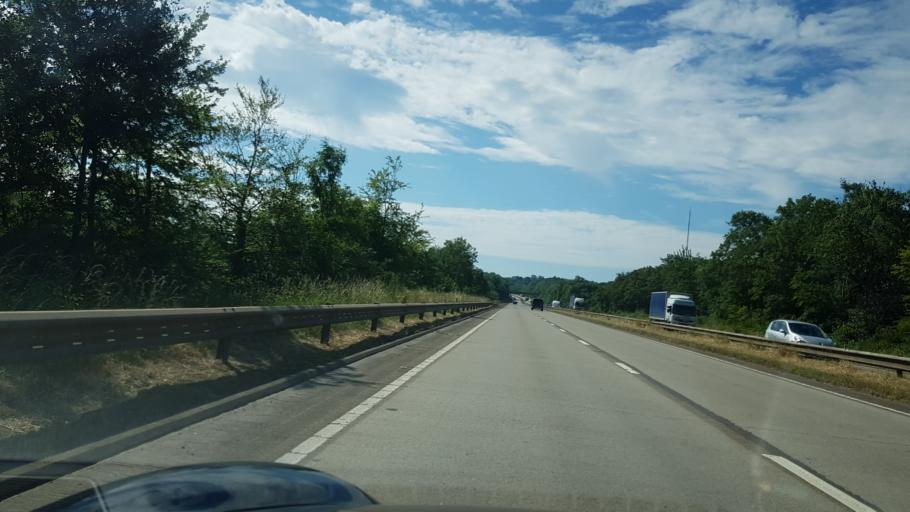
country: GB
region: Wales
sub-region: Cardiff
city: Radyr
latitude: 51.4799
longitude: -3.2818
